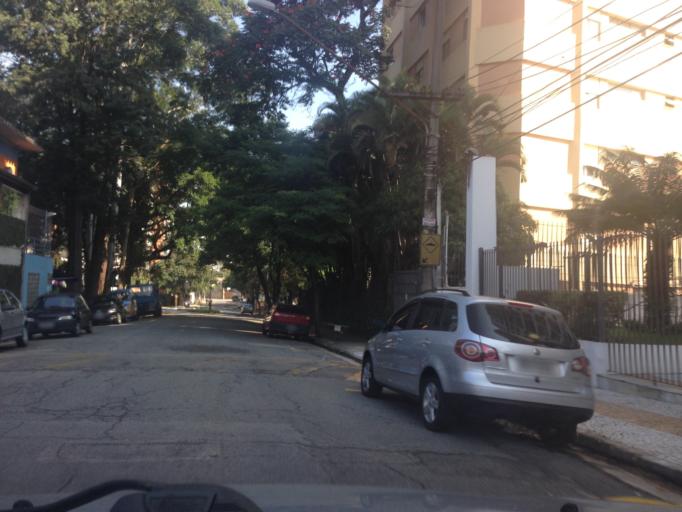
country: BR
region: Sao Paulo
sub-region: Sao Paulo
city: Sao Paulo
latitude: -23.5433
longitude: -46.7036
